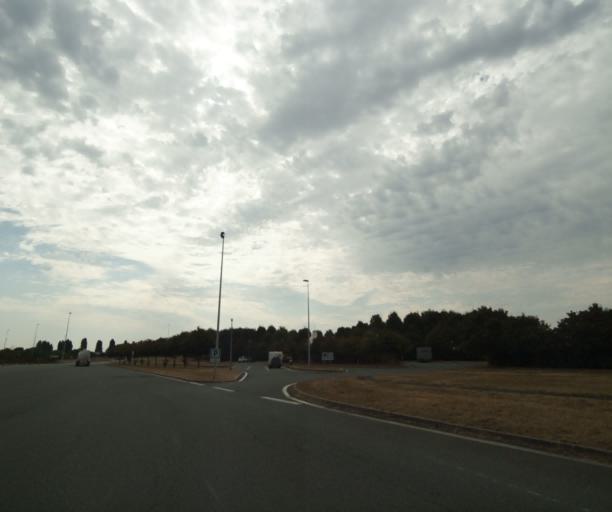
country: FR
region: Poitou-Charentes
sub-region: Departement de la Charente-Maritime
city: Tonnay-Charente
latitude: 45.9546
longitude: -0.8810
